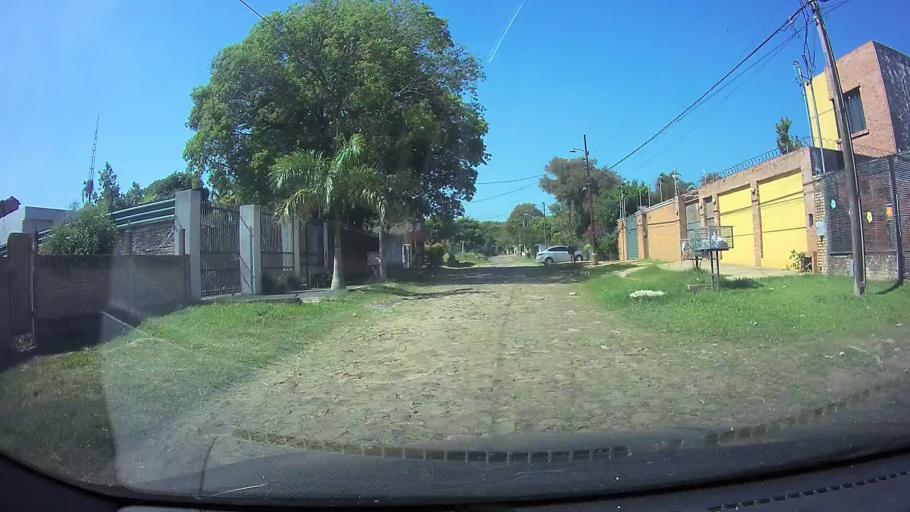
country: PY
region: Central
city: Fernando de la Mora
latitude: -25.2833
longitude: -57.5365
